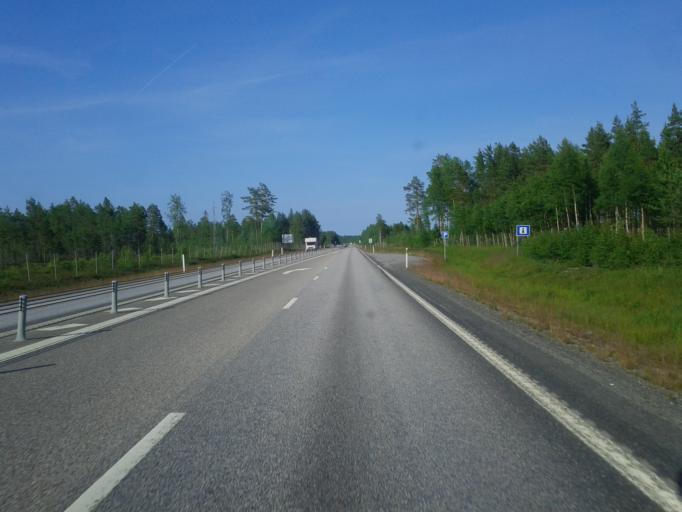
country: SE
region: Vaesterbotten
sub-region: Umea Kommun
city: Saevar
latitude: 63.9587
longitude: 20.6809
